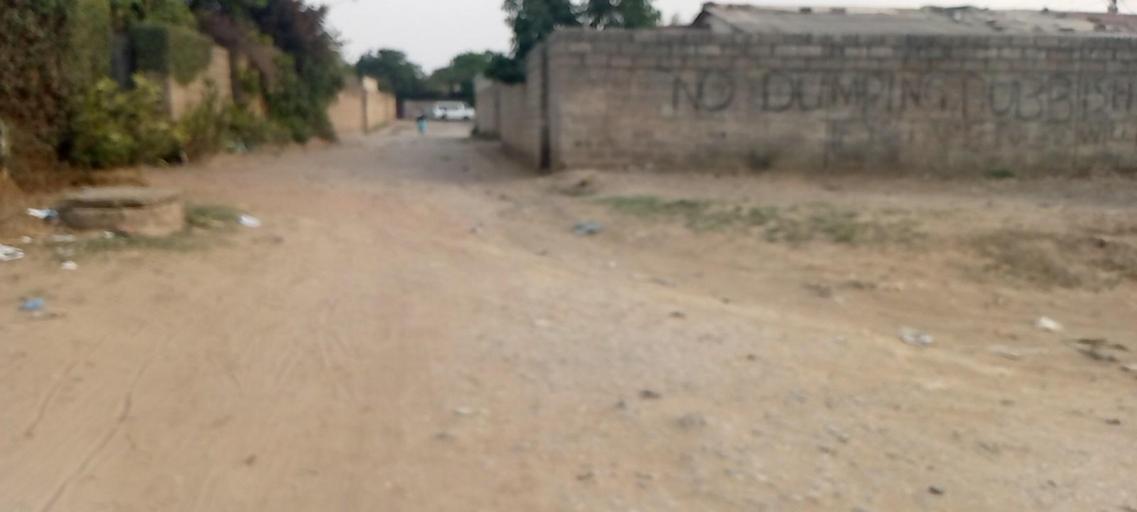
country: ZM
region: Lusaka
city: Lusaka
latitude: -15.4030
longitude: 28.3463
